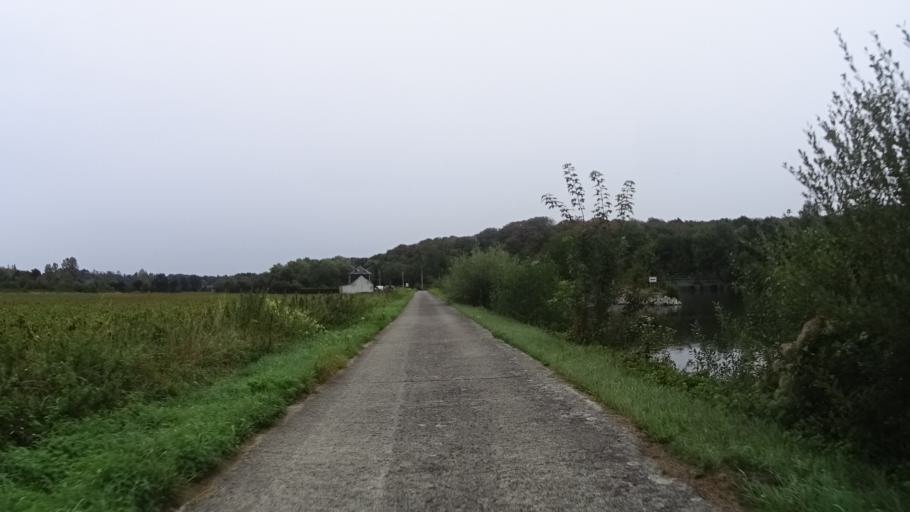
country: BE
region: Wallonia
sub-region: Province du Hainaut
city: Lobbes
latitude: 50.3213
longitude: 4.2283
